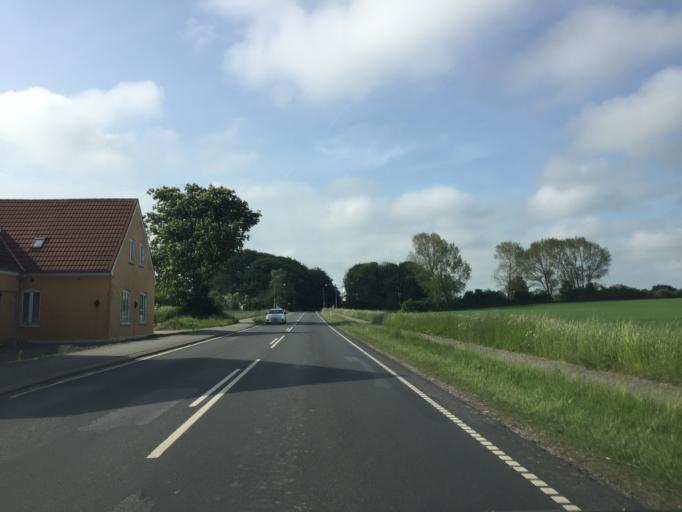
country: DK
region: South Denmark
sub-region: Svendborg Kommune
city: Thuro By
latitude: 55.1250
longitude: 10.7292
